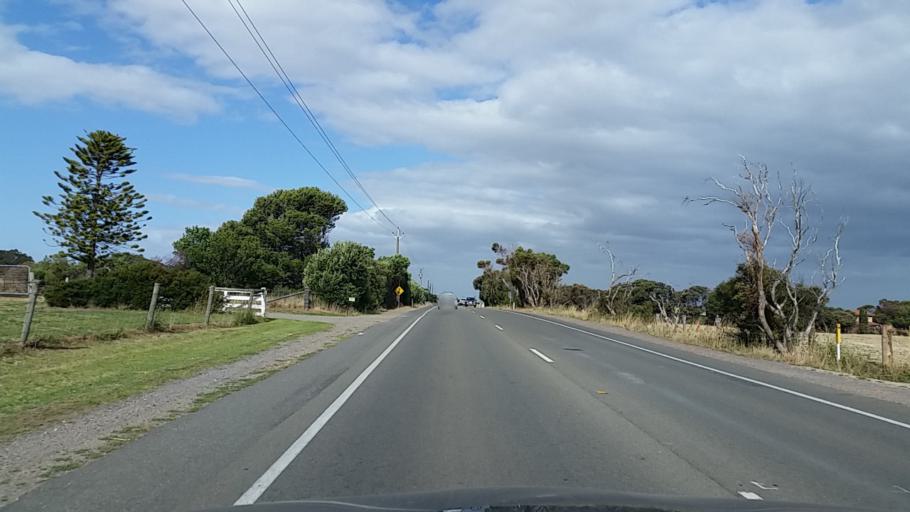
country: AU
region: South Australia
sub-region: Alexandrina
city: Port Elliot
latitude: -35.5121
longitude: 138.6963
